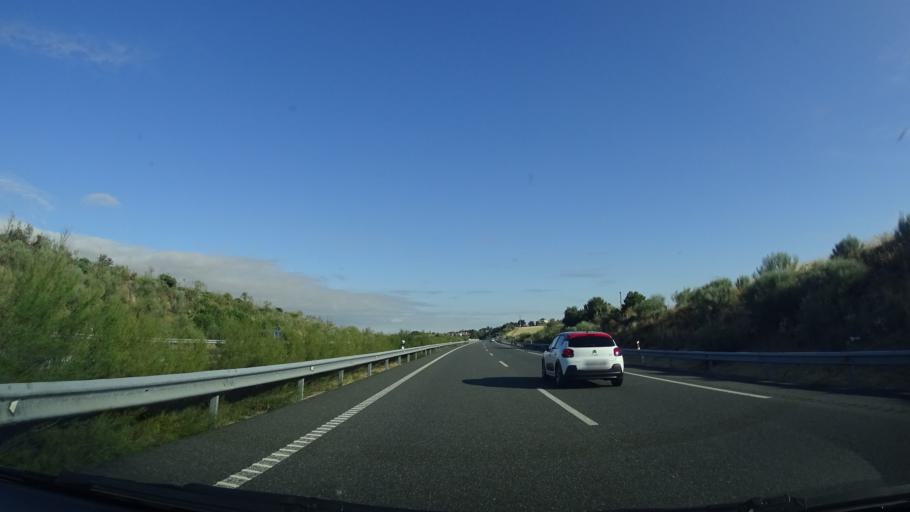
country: ES
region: Castille and Leon
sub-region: Provincia de Segovia
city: Labajos
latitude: 40.8490
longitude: -4.5431
